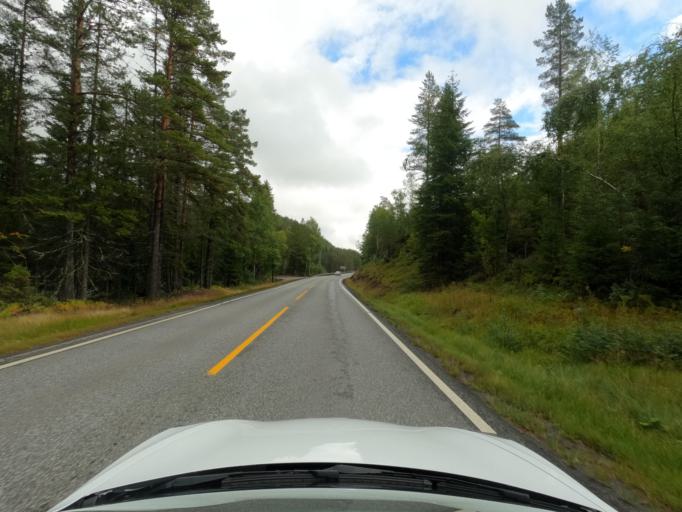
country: NO
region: Telemark
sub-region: Notodden
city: Notodden
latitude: 59.6061
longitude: 9.4366
